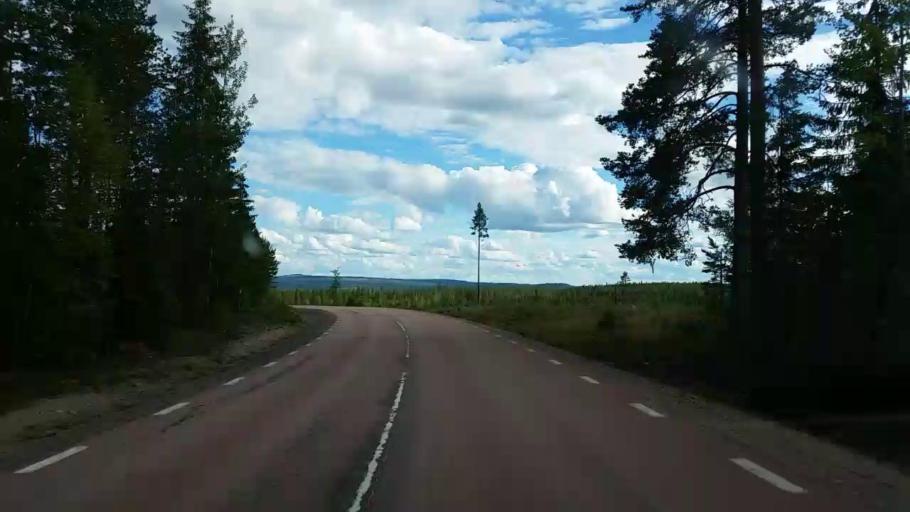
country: SE
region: Gaevleborg
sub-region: Ljusdals Kommun
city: Farila
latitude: 61.9615
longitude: 15.8770
